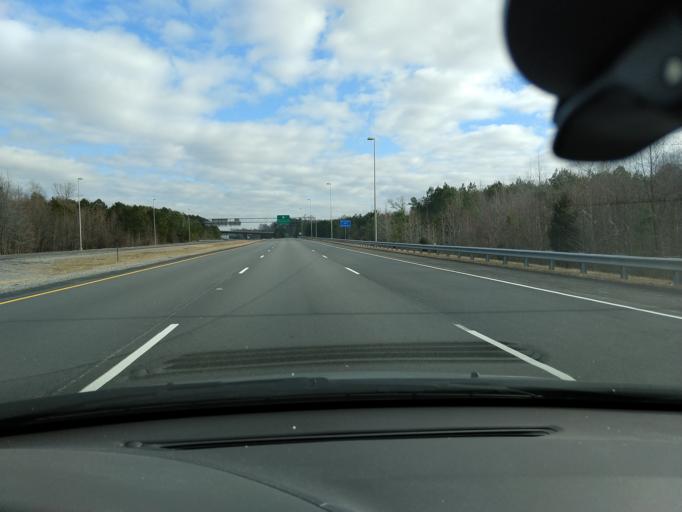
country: US
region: Virginia
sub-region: Chesterfield County
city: Bensley
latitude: 37.4482
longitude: -77.4014
